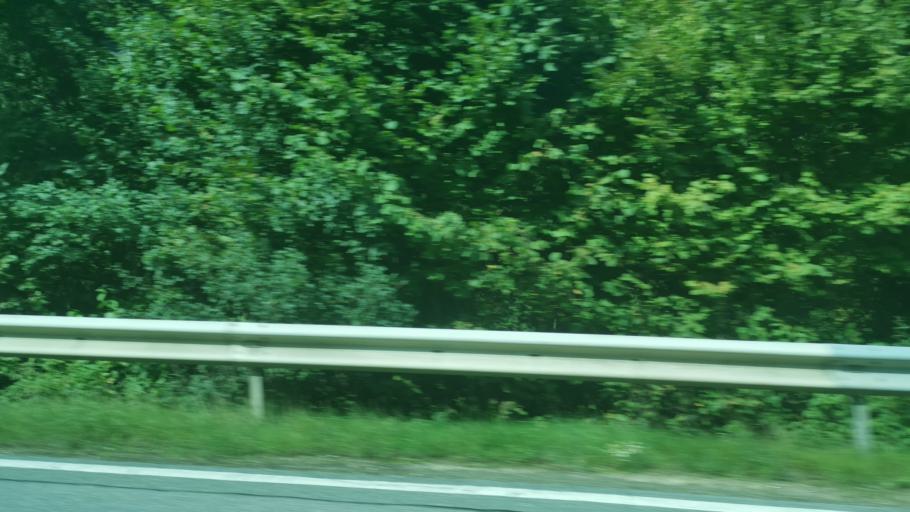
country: DE
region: Bavaria
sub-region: Upper Palatinate
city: Pemfling
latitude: 49.2857
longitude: 12.6258
